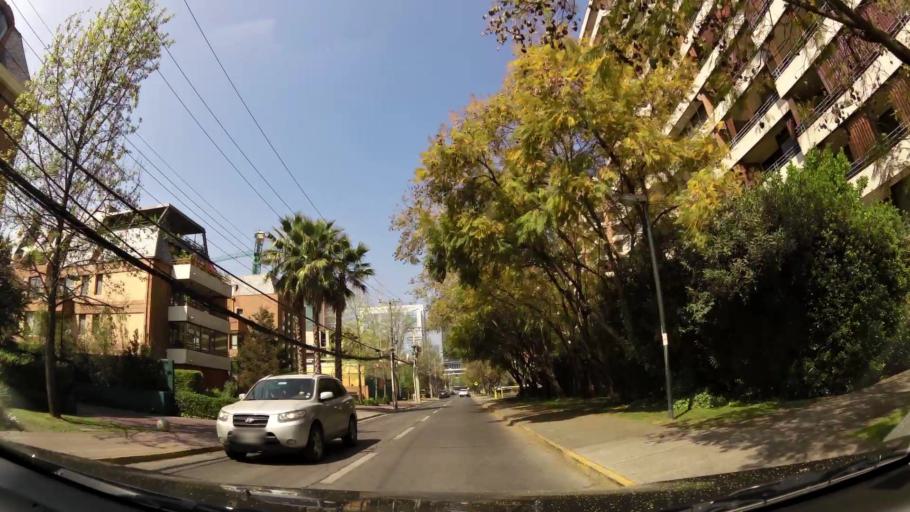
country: CL
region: Santiago Metropolitan
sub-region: Provincia de Santiago
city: Villa Presidente Frei, Nunoa, Santiago, Chile
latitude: -33.3972
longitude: -70.5769
